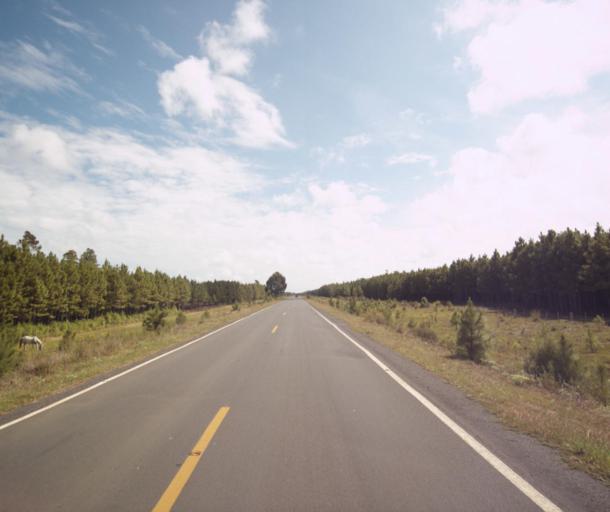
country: BR
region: Rio Grande do Sul
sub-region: Sao Lourenco Do Sul
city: Sao Lourenco do Sul
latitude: -31.4483
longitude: -51.2092
